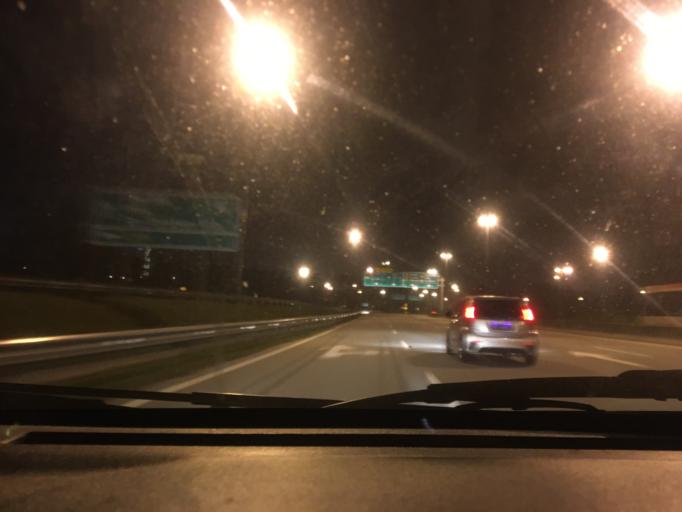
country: MY
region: Selangor
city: Kampong Baharu Balakong
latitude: 2.9854
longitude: 101.7310
